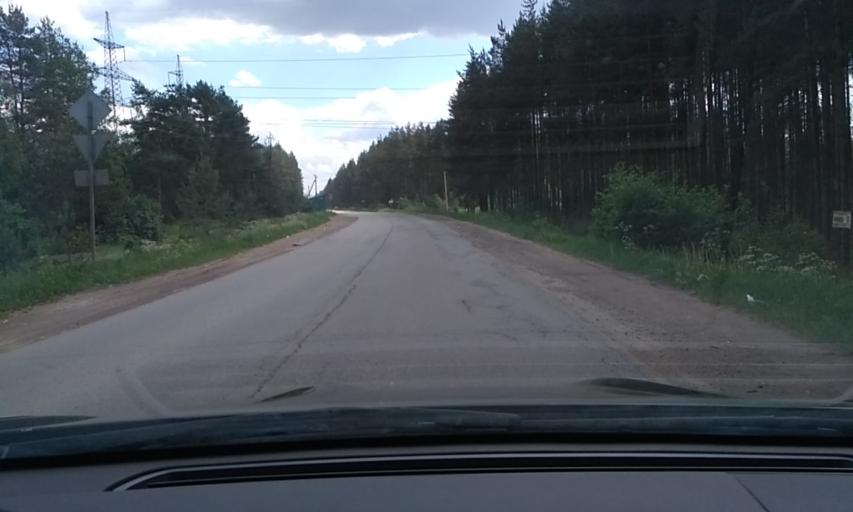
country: RU
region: Leningrad
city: Imeni Sverdlova
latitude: 59.8566
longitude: 30.6731
